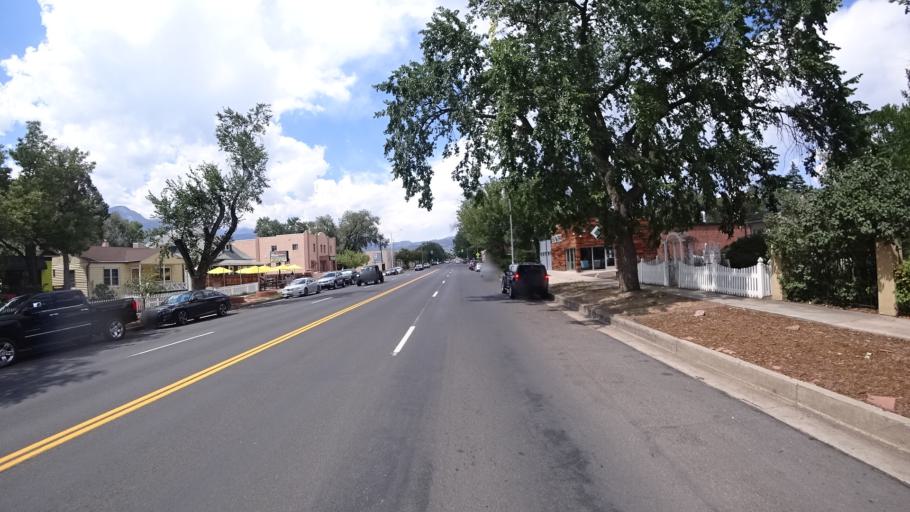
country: US
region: Colorado
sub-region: El Paso County
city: Colorado Springs
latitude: 38.8449
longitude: -104.8588
